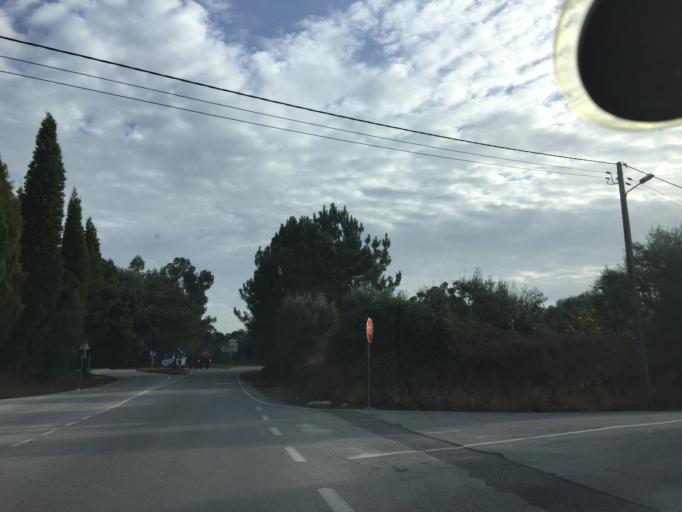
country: PT
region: Aveiro
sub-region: Anadia
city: Arcos
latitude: 40.4536
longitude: -8.4332
